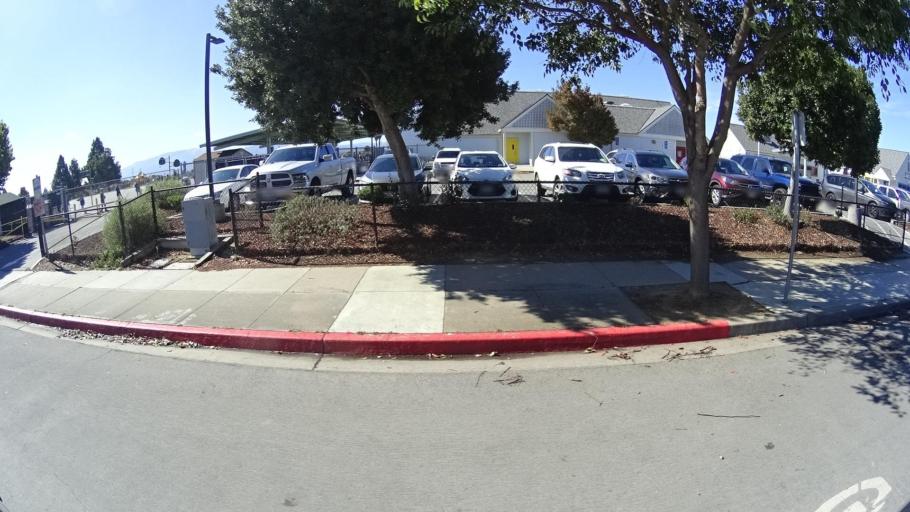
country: US
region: California
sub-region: Monterey County
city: Boronda
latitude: 36.6916
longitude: -121.6629
